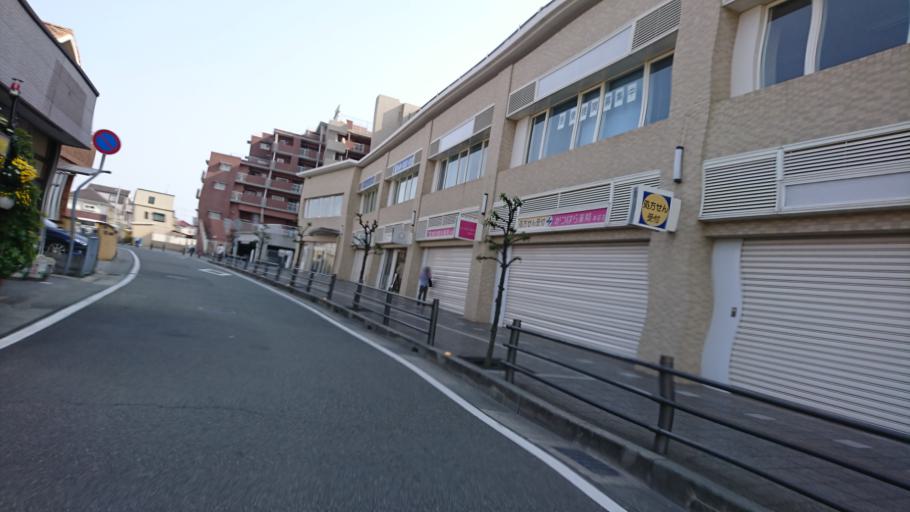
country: JP
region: Hyogo
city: Kakogawacho-honmachi
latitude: 34.7167
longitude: 134.8686
